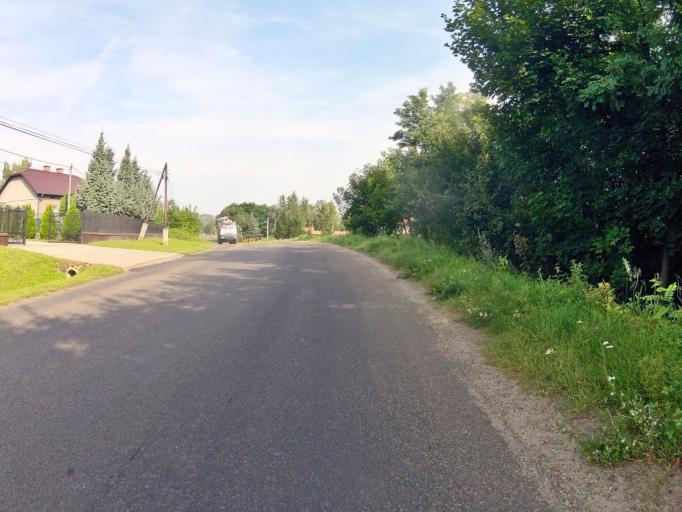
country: PL
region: Subcarpathian Voivodeship
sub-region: Powiat jasielski
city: Kolaczyce
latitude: 49.7852
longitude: 21.4035
